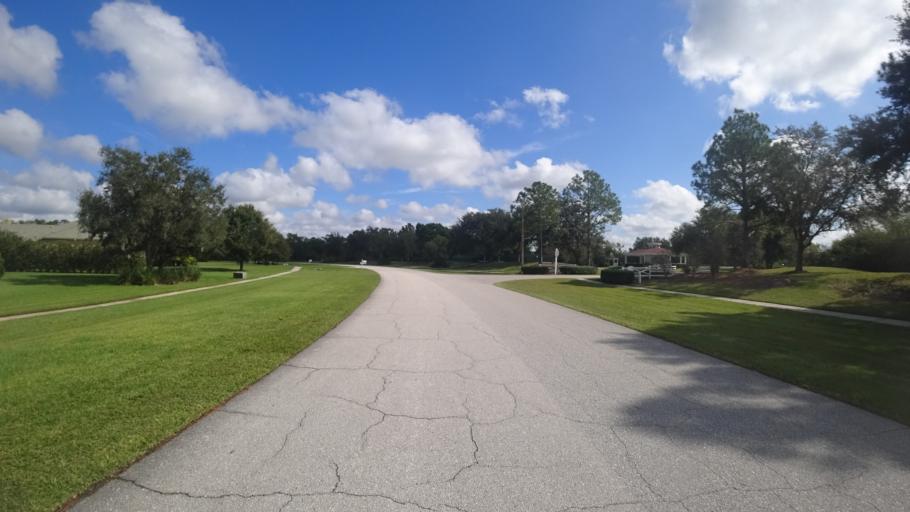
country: US
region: Florida
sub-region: Sarasota County
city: Fruitville
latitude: 27.3978
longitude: -82.3103
